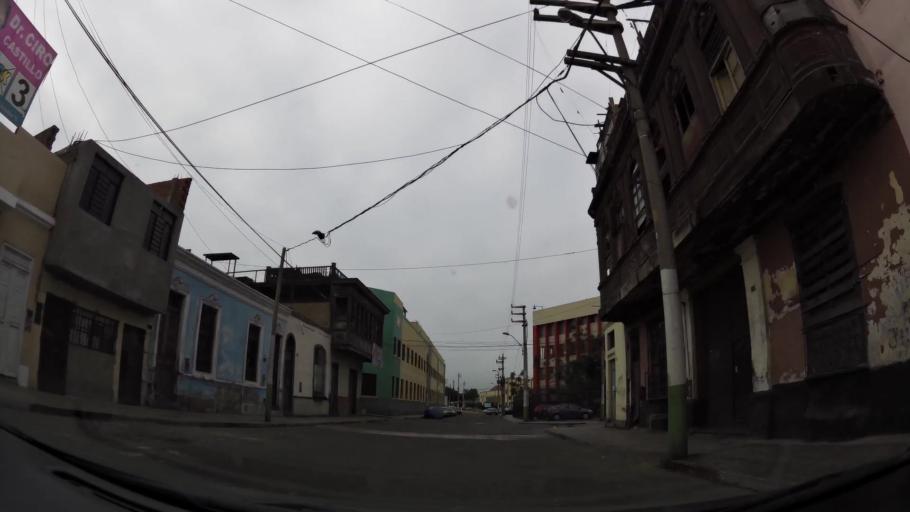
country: PE
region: Callao
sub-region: Callao
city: Callao
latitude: -12.0568
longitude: -77.1435
